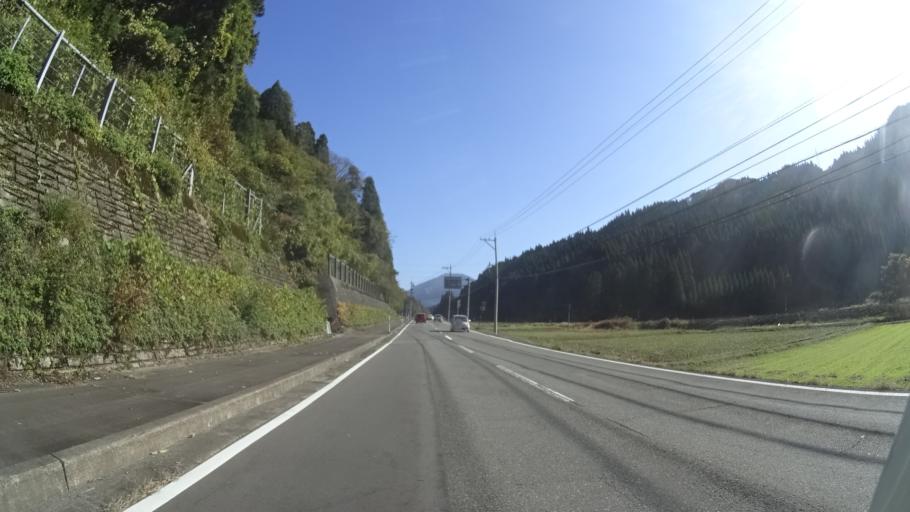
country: JP
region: Fukui
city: Ono
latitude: 36.0075
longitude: 136.3963
